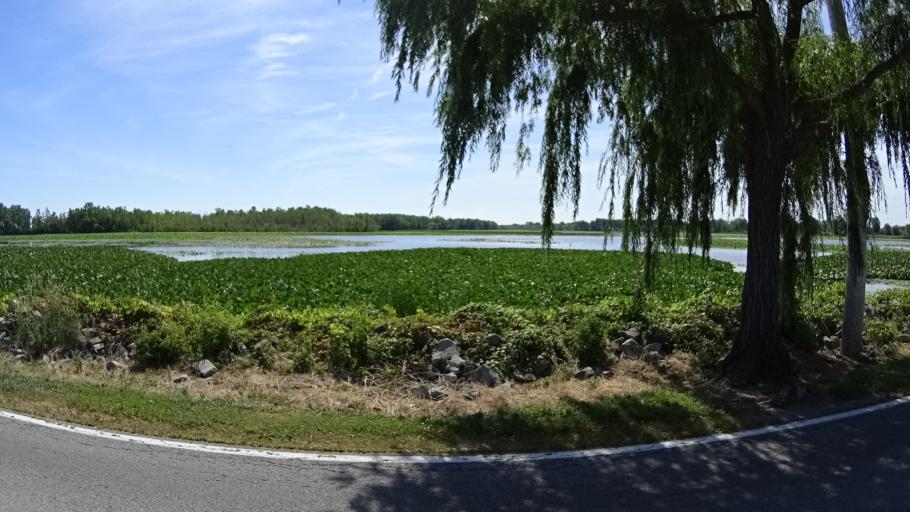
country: US
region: Ohio
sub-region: Erie County
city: Huron
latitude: 41.4275
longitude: -82.6240
